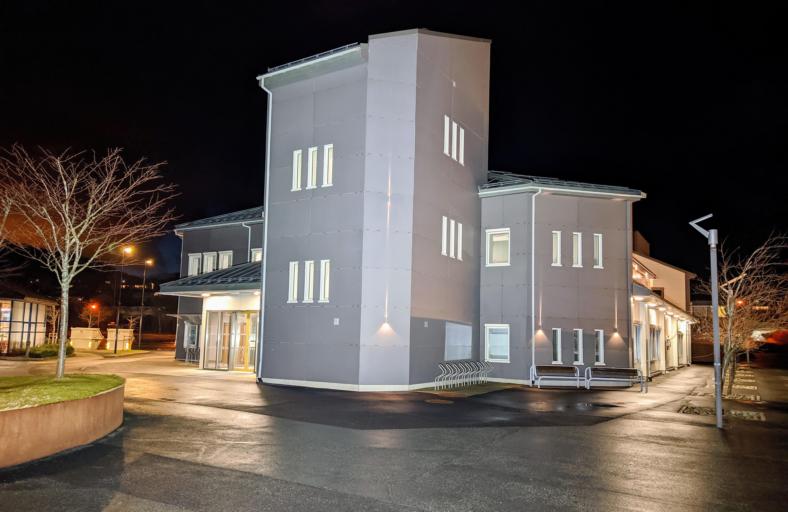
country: NO
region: Rogaland
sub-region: Vindafjord
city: Olen
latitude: 59.8610
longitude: 5.7560
